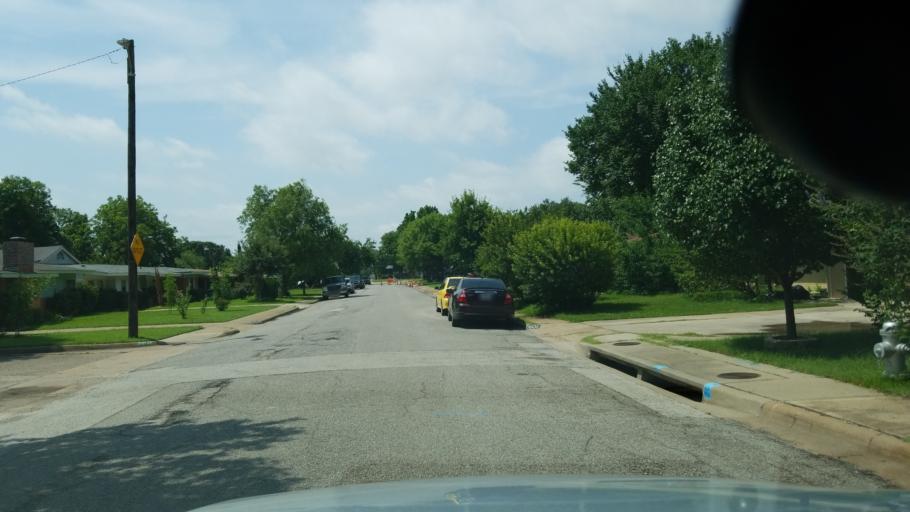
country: US
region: Texas
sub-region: Dallas County
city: Irving
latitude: 32.8312
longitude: -96.9480
